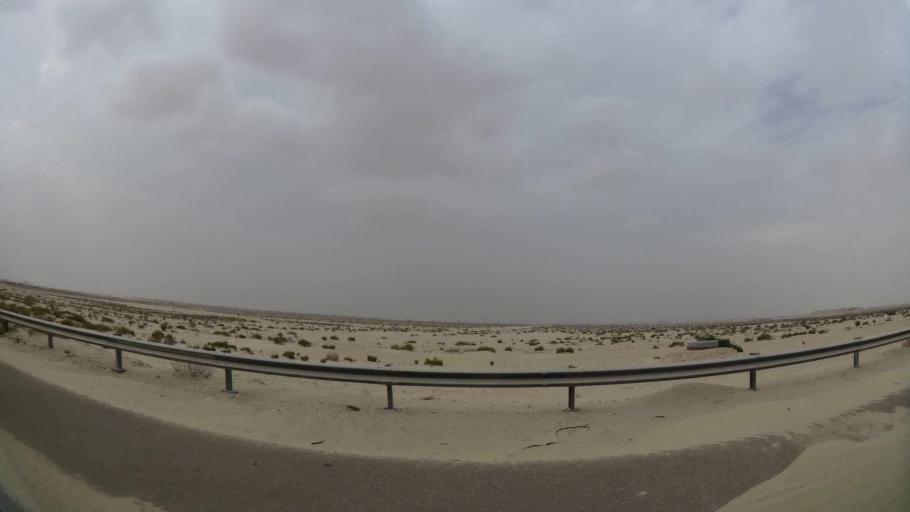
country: AE
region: Abu Dhabi
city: Abu Dhabi
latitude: 24.3932
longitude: 54.6826
